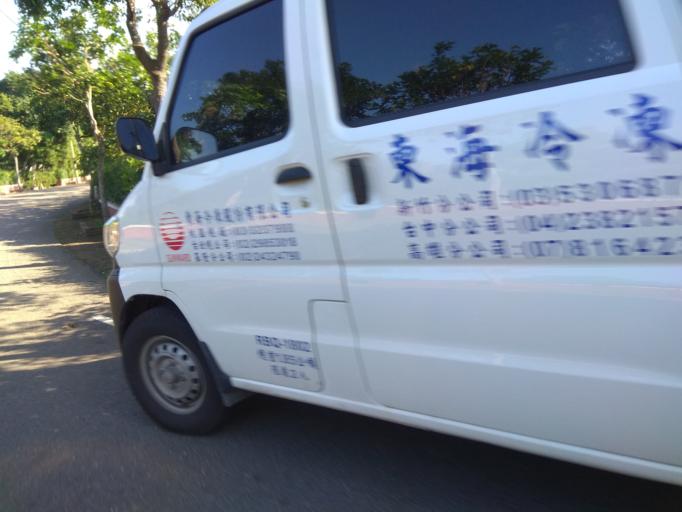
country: TW
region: Taiwan
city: Taoyuan City
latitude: 25.0512
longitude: 121.2278
